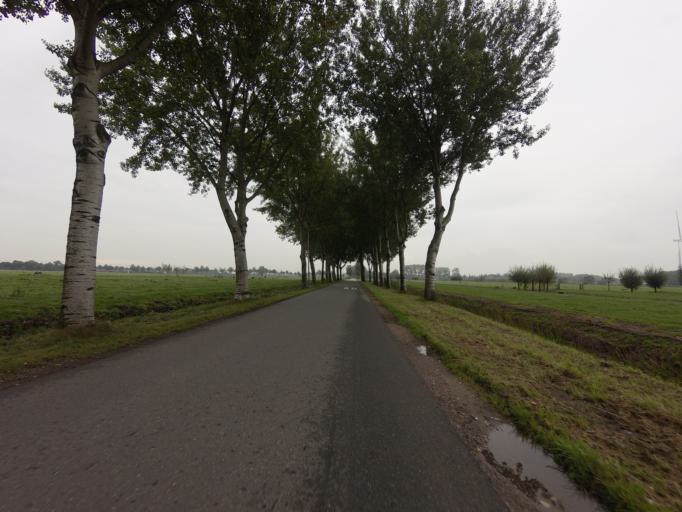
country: NL
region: Utrecht
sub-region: Gemeente Vianen
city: Vianen
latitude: 51.9738
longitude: 5.1166
